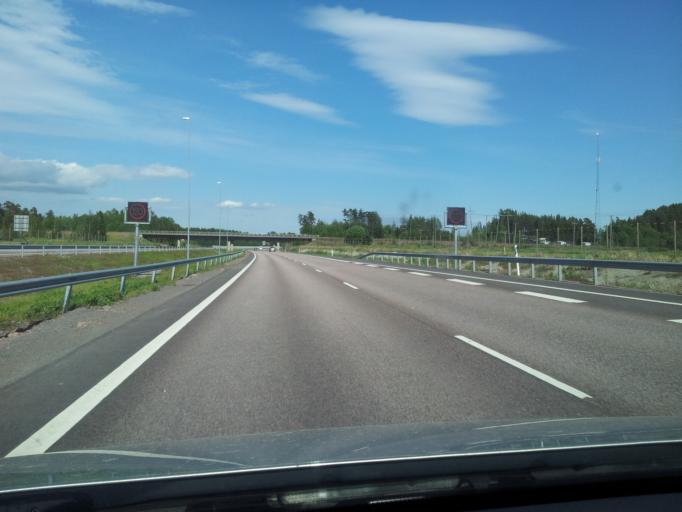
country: FI
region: Uusimaa
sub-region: Loviisa
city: Lovisa
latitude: 60.4628
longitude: 26.2037
